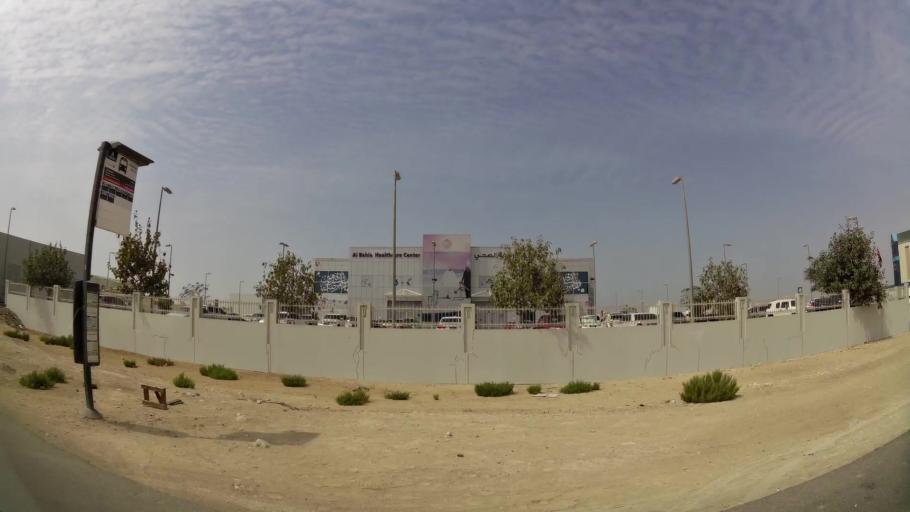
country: AE
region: Abu Dhabi
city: Abu Dhabi
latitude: 24.5199
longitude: 54.6692
